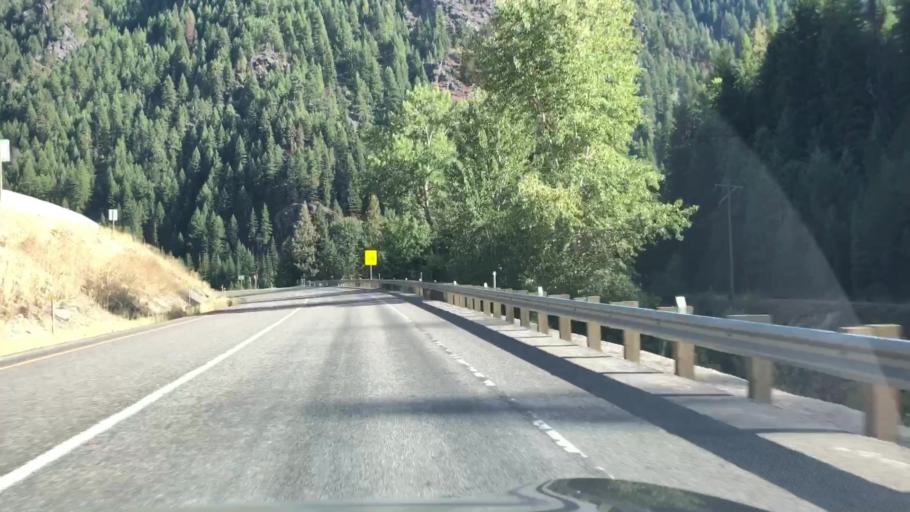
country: US
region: Montana
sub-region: Sanders County
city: Thompson Falls
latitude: 47.3138
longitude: -115.2356
